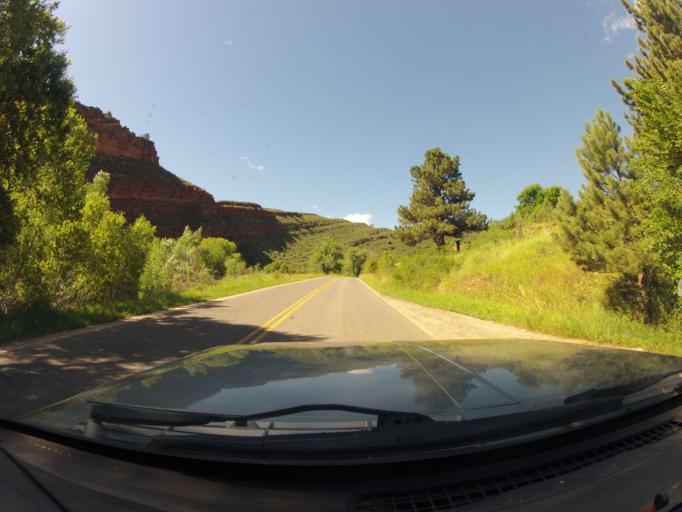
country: US
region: Colorado
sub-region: Larimer County
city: Laporte
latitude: 40.5058
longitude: -105.2328
